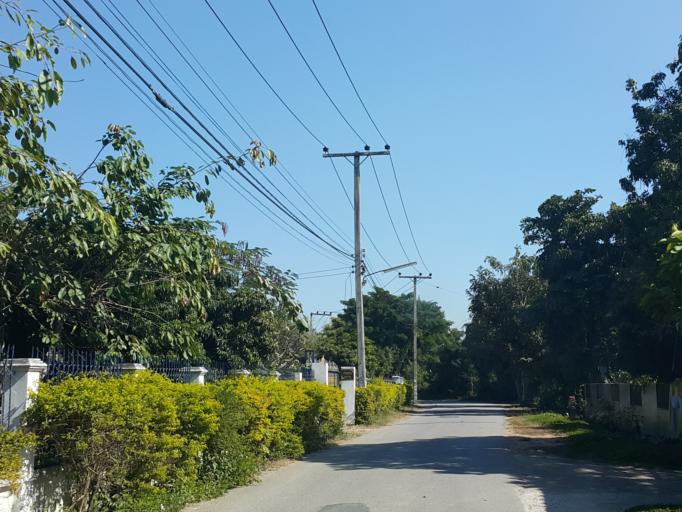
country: TH
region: Chiang Mai
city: San Sai
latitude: 18.8860
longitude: 98.9908
